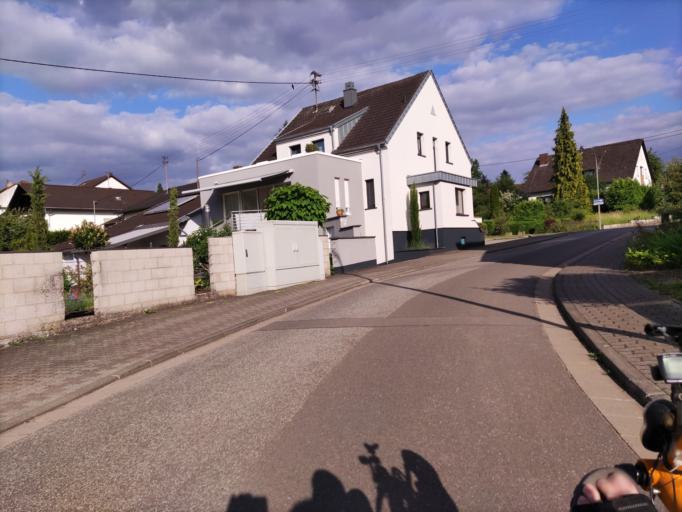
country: DE
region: Saarland
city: Rehlingen-Siersburg
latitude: 49.3643
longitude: 6.6625
